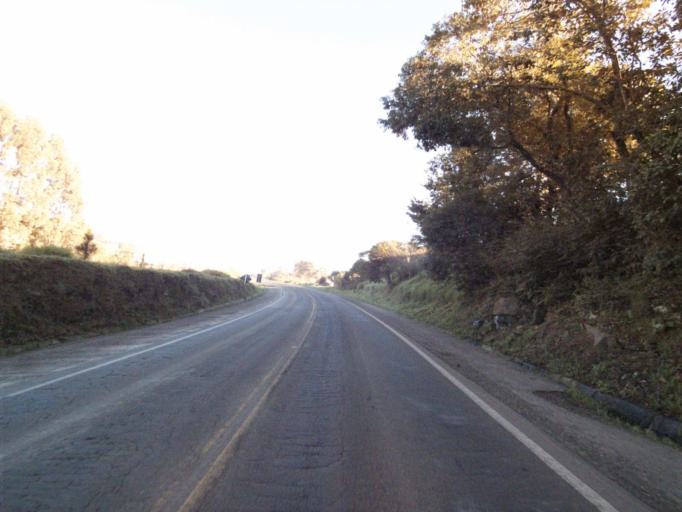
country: BR
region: Santa Catarina
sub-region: Sao Lourenco Do Oeste
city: Sao Lourenco dOeste
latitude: -26.7786
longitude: -53.1987
